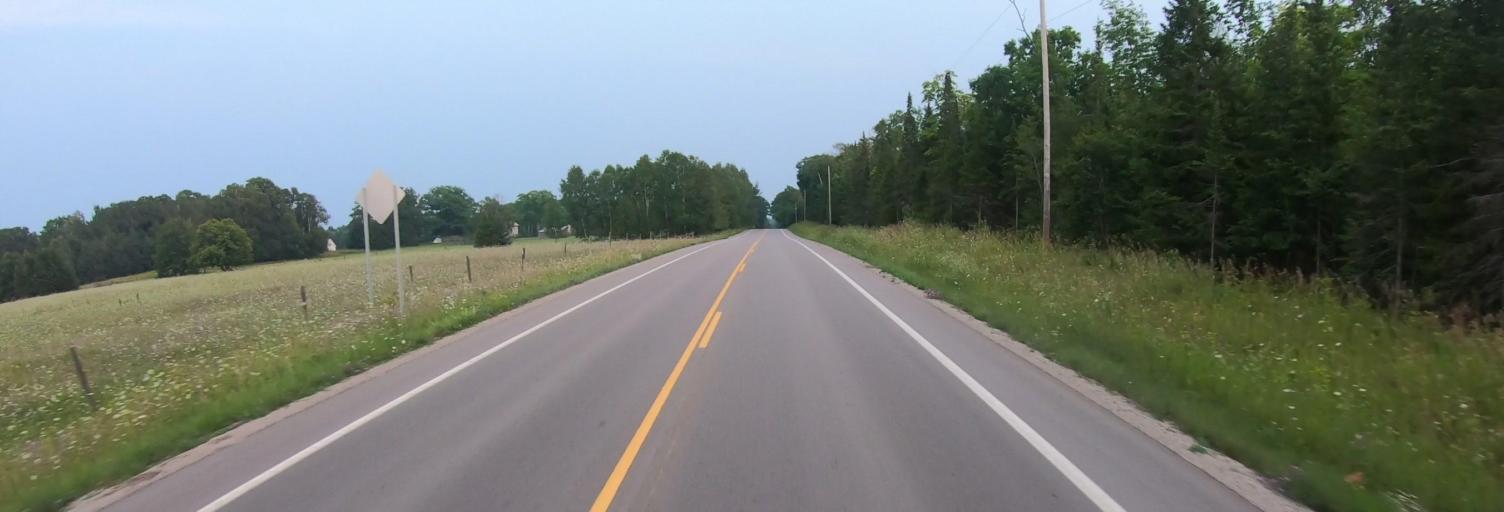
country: US
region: Michigan
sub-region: Mackinac County
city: Saint Ignace
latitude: 45.7801
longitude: -84.7733
